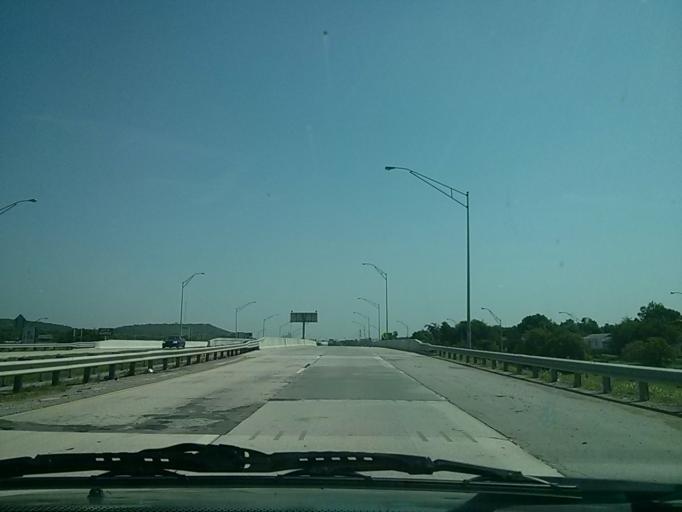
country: US
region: Oklahoma
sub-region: Tulsa County
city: Oakhurst
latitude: 36.0968
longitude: -96.0303
